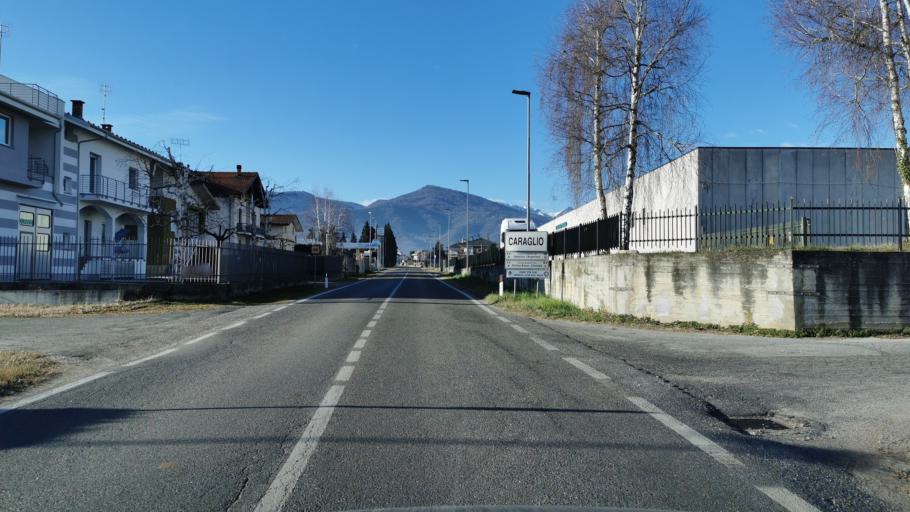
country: IT
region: Piedmont
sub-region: Provincia di Cuneo
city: Caraglio
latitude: 44.4259
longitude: 7.4430
